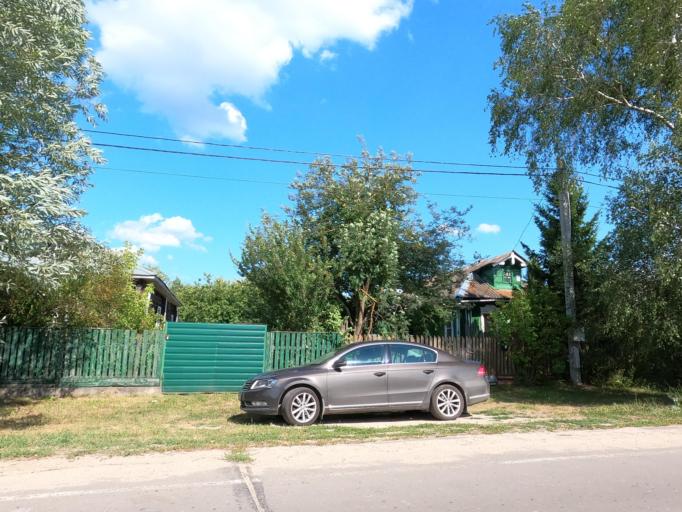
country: RU
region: Moskovskaya
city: Peski
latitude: 55.2268
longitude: 38.7509
